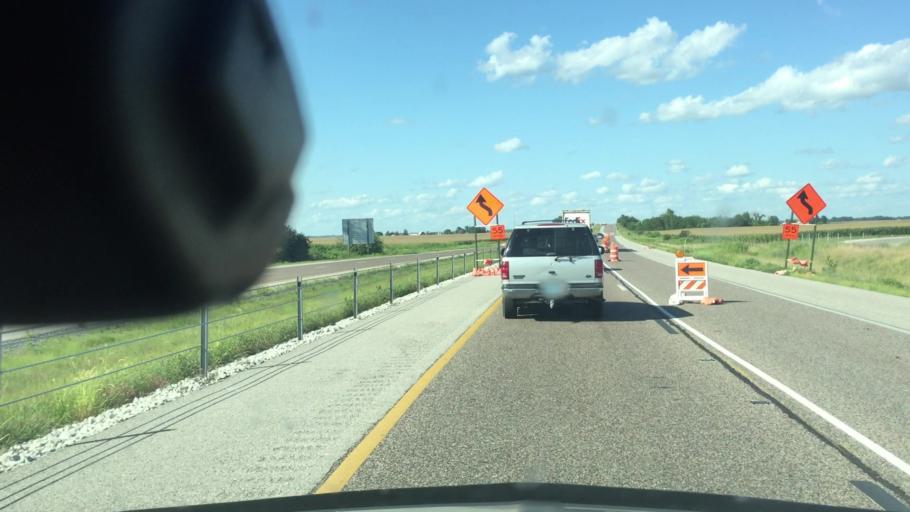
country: US
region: Illinois
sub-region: Madison County
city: Edwardsville
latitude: 38.8167
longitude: -89.8888
